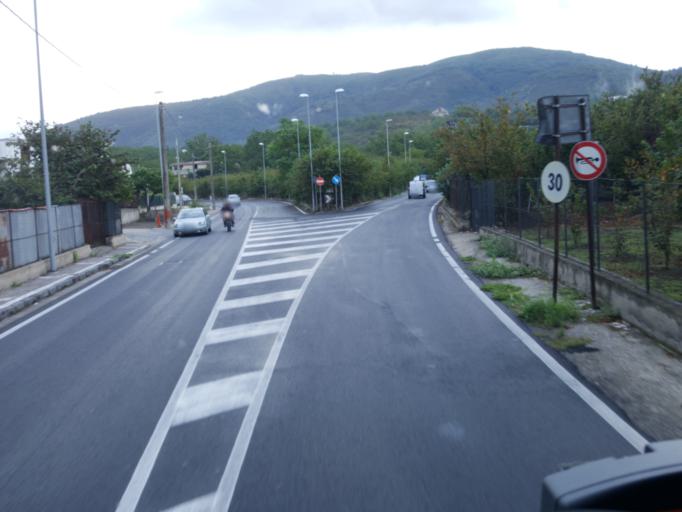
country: IT
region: Campania
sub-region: Provincia di Napoli
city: Palma Campania
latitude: 40.8779
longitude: 14.5598
